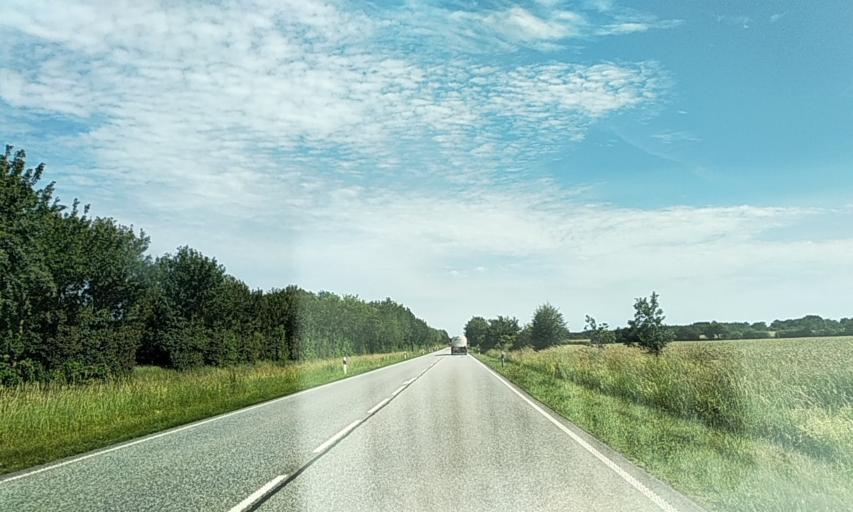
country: DE
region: Schleswig-Holstein
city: Kropp
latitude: 54.4211
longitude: 9.5304
